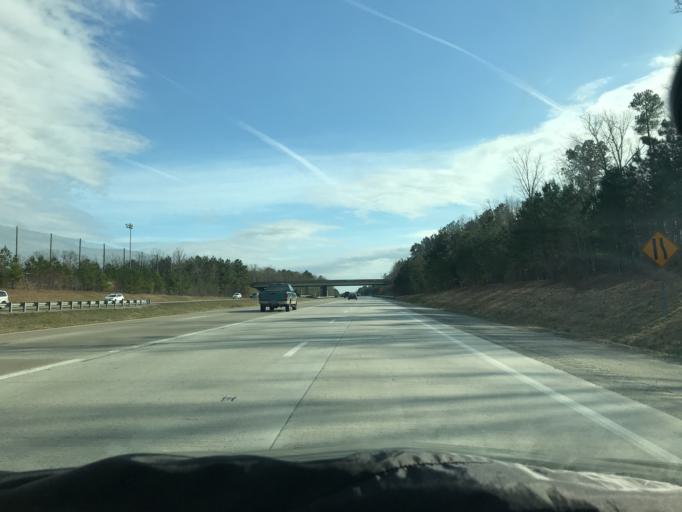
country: US
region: Virginia
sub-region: Chesterfield County
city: Brandermill
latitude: 37.4530
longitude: -77.6377
